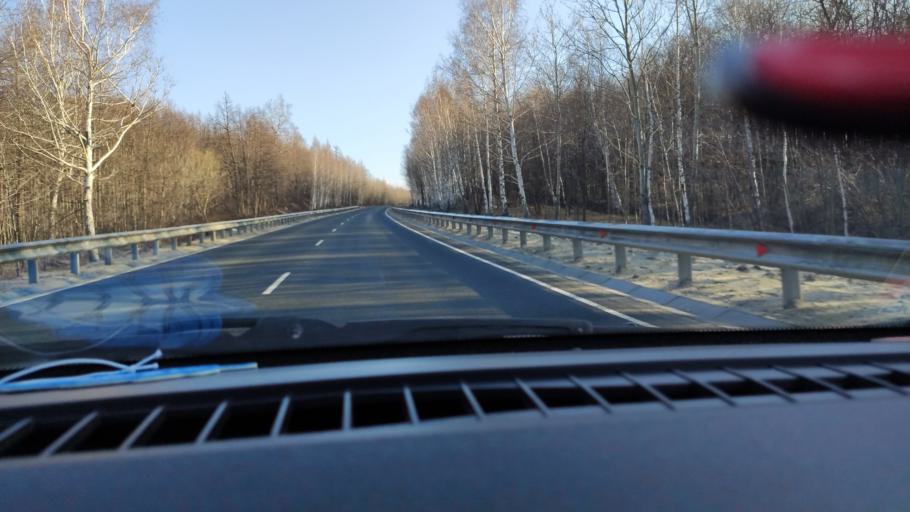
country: RU
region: Saratov
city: Khvalynsk
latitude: 52.4461
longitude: 48.0102
